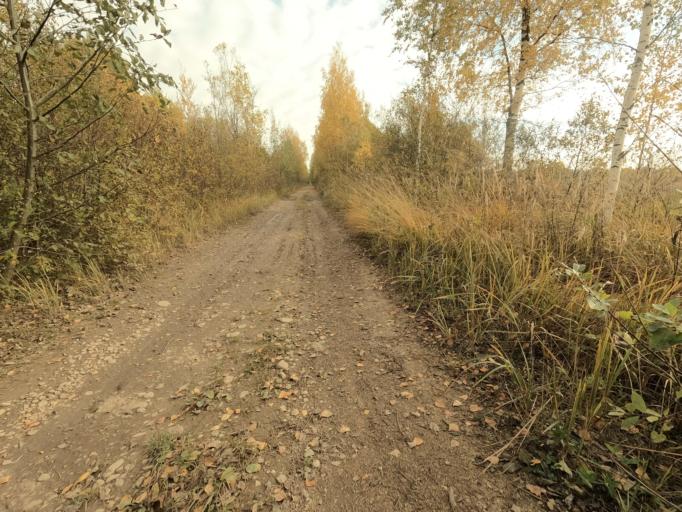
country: RU
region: Novgorod
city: Pankovka
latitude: 58.8798
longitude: 30.8075
